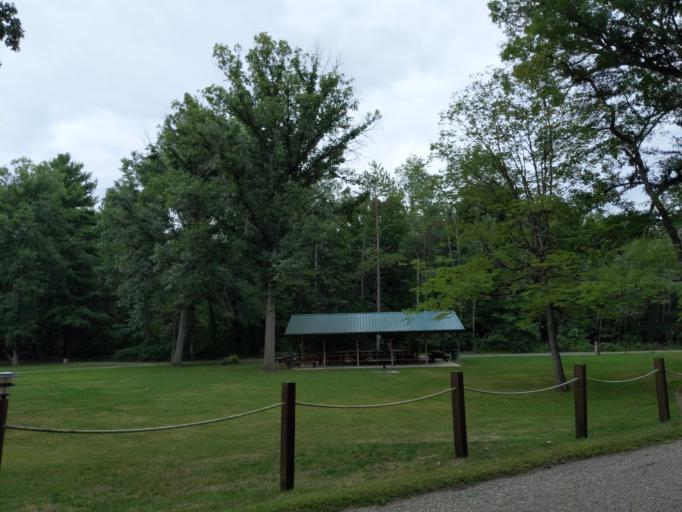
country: US
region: Michigan
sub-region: Ionia County
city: Ionia
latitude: 42.9759
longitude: -85.1205
